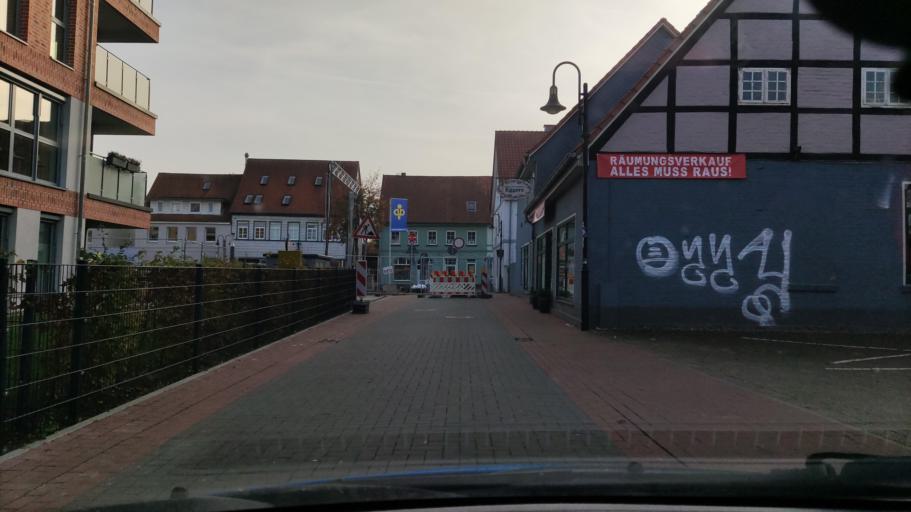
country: DE
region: Lower Saxony
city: Walsrode
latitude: 52.8624
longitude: 9.5941
